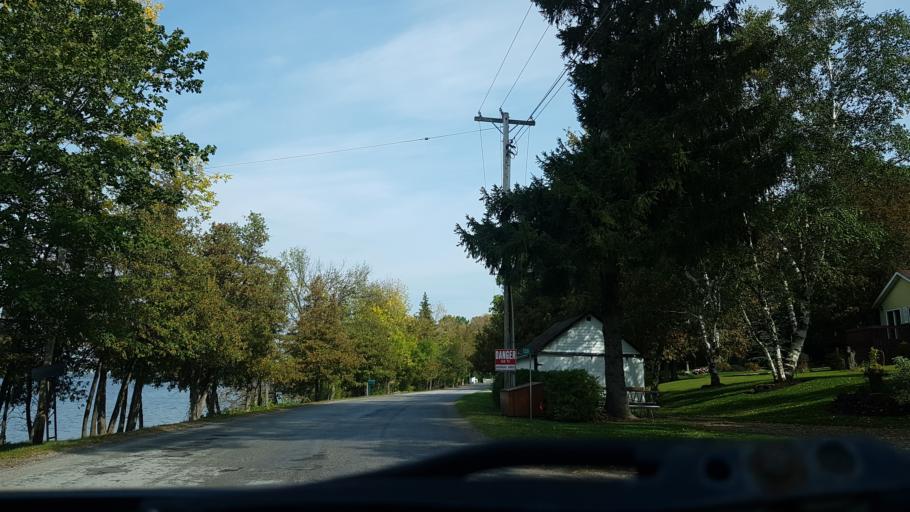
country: CA
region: Ontario
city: Orillia
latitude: 44.6493
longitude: -79.1042
